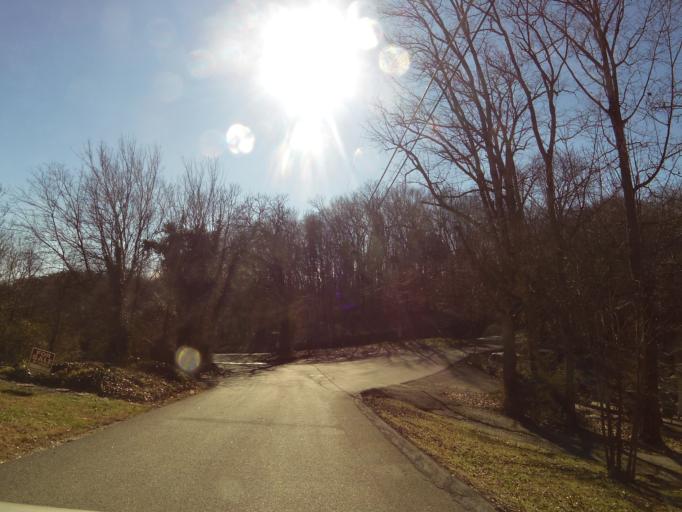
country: US
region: Tennessee
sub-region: Knox County
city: Knoxville
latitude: 35.9379
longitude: -83.8701
